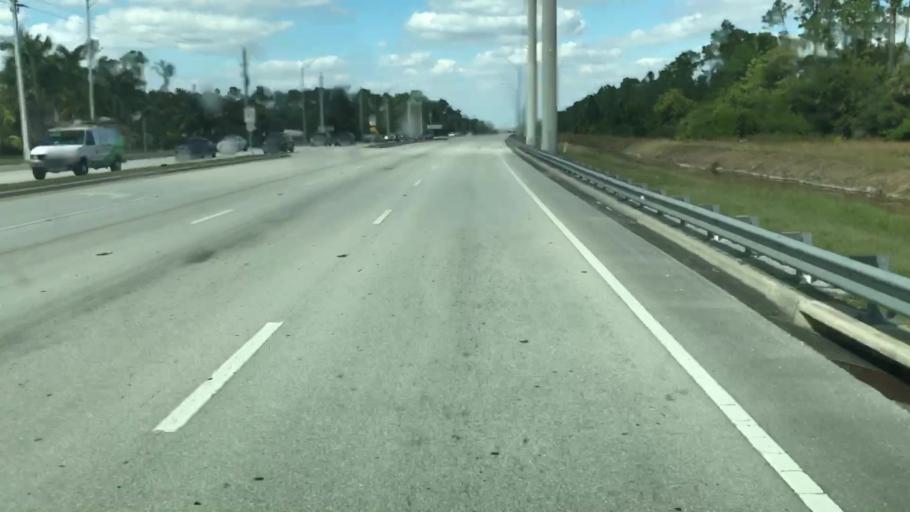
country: US
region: Florida
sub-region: Collier County
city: Vineyards
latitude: 26.2315
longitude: -81.6877
